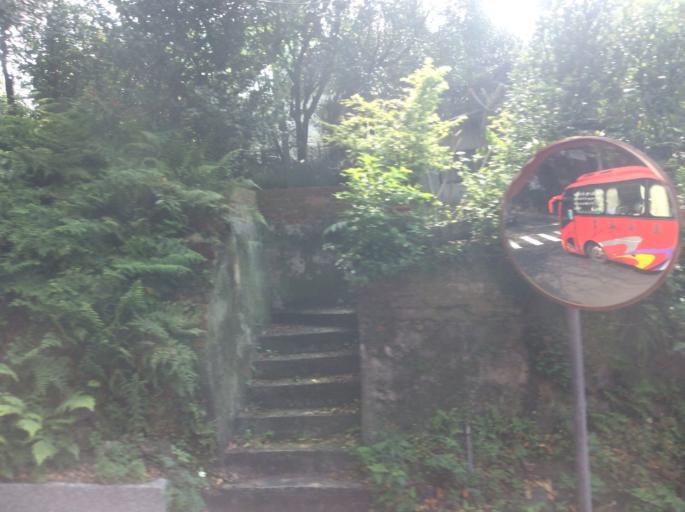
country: TW
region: Taipei
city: Taipei
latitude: 25.1490
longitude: 121.5495
